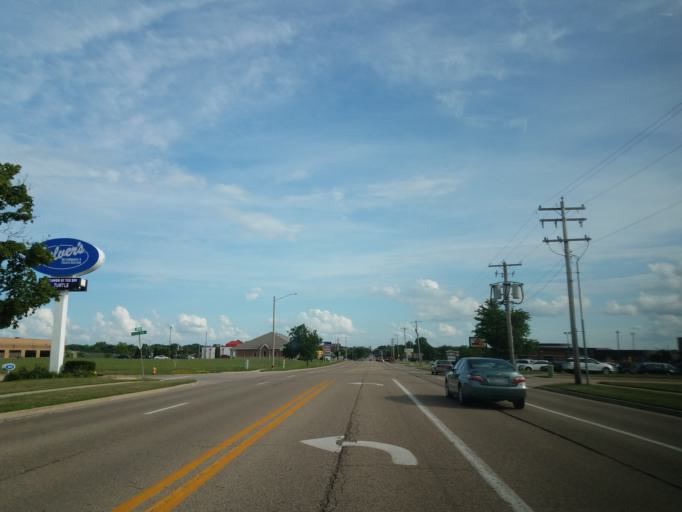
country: US
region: Illinois
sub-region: McLean County
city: Bloomington
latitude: 40.4864
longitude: -88.9432
